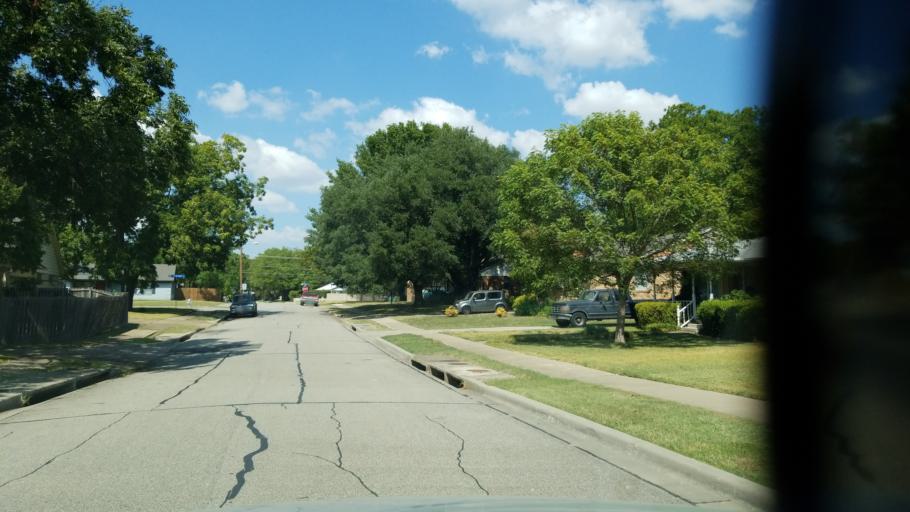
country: US
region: Texas
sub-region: Dallas County
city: Richardson
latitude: 32.9611
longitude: -96.7590
